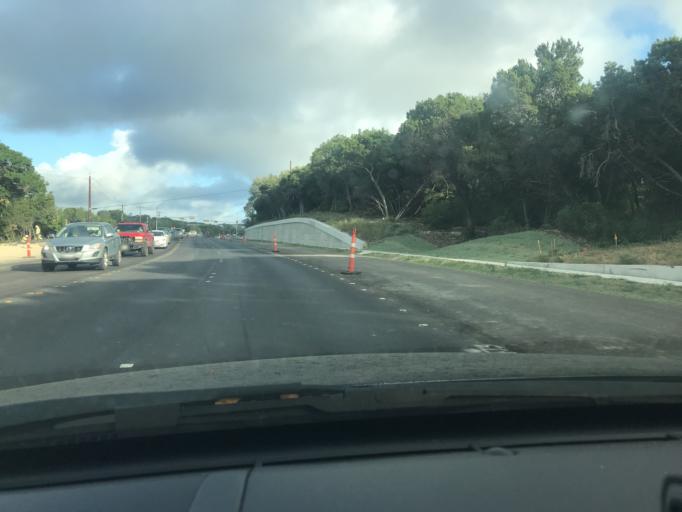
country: US
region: Texas
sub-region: Travis County
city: West Lake Hills
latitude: 30.2868
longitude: -97.8133
